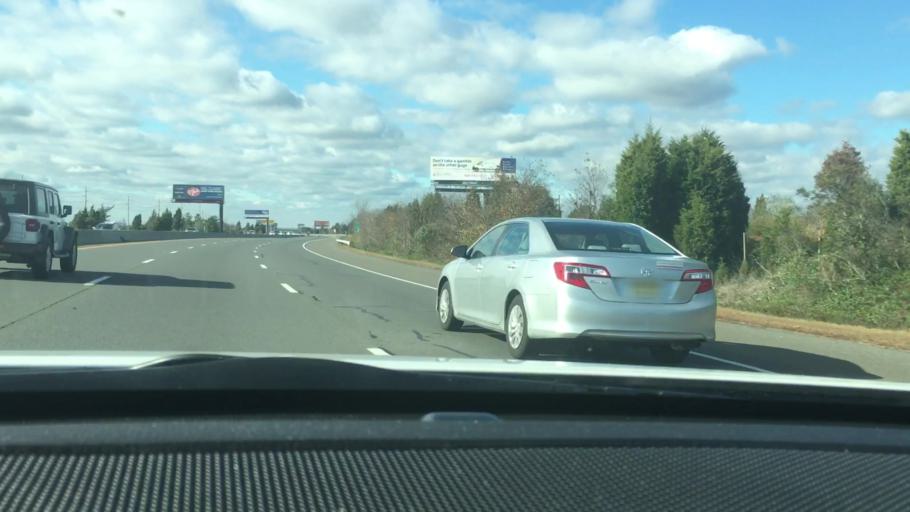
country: US
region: New Jersey
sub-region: Atlantic County
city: Ventnor City
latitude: 39.3681
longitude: -74.4626
